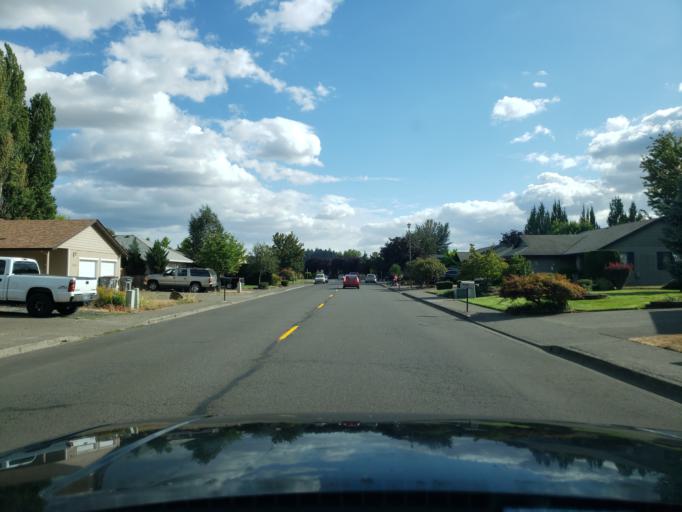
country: US
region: Oregon
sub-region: Yamhill County
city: McMinnville
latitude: 45.2029
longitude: -123.2197
